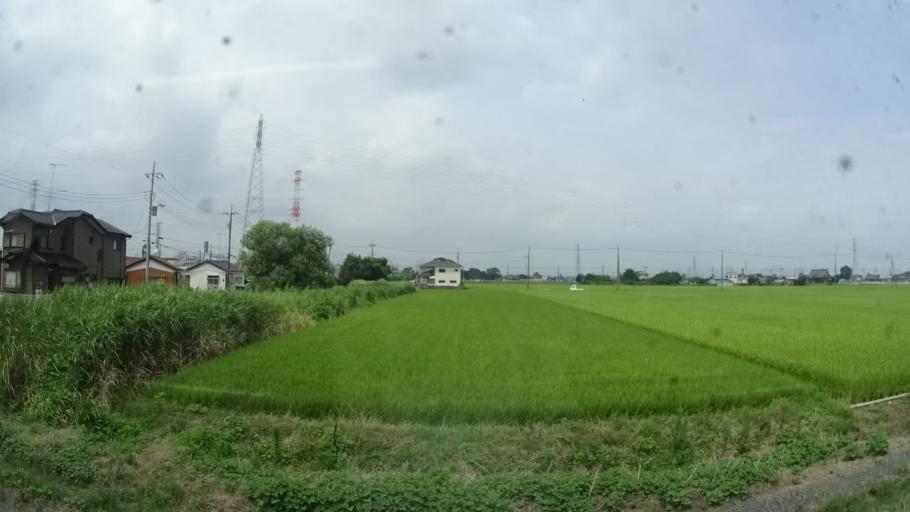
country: JP
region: Ibaraki
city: Shimodate
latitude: 36.3115
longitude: 139.9718
